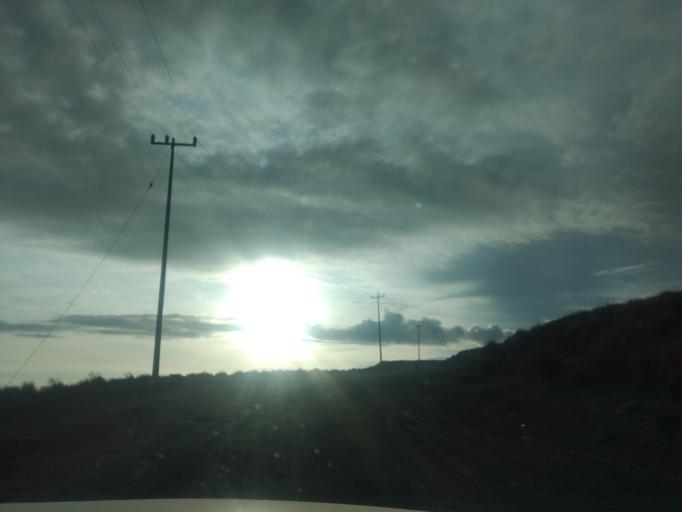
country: MX
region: Mexico
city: Cerro La Calera
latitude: 19.1287
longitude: -99.7648
